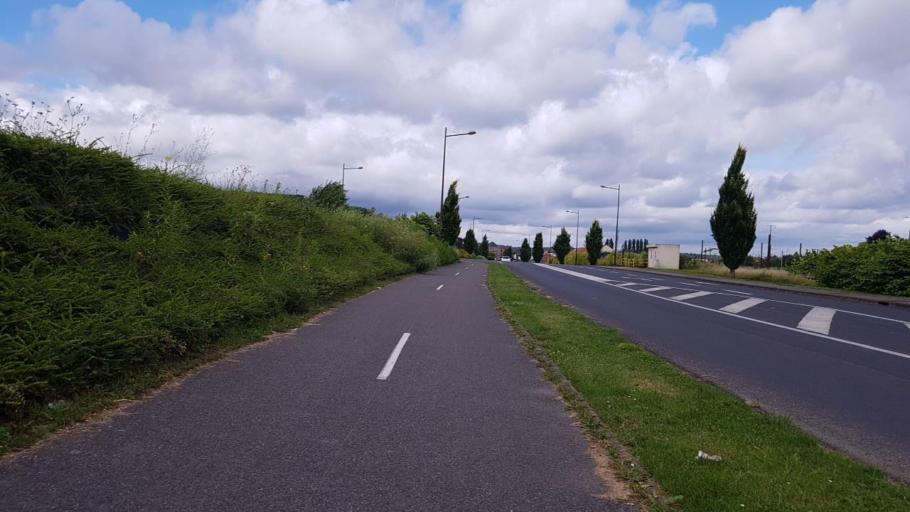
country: FR
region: Picardie
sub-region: Departement de l'Aisne
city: Hirson
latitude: 49.9113
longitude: 4.0782
